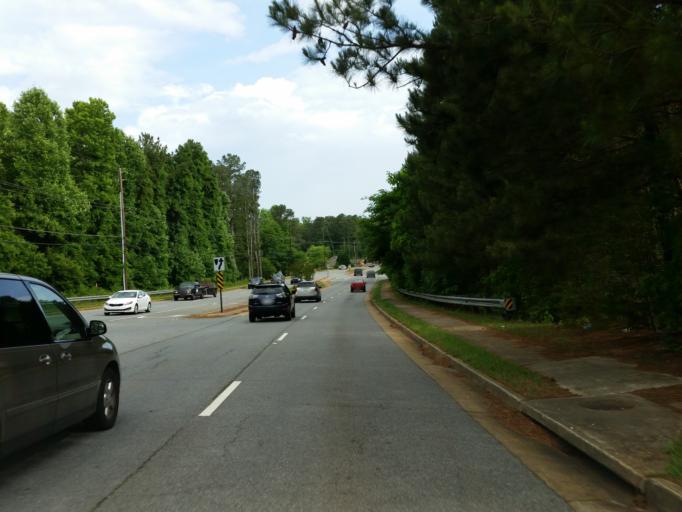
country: US
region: Georgia
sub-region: Cobb County
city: Marietta
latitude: 34.0065
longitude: -84.4874
